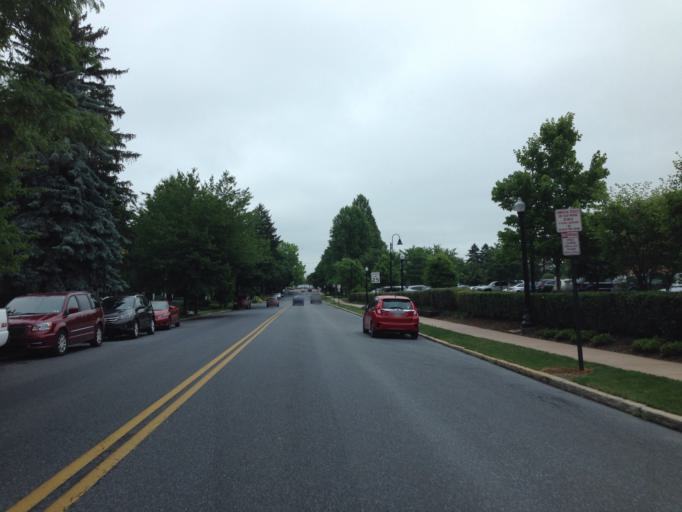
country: US
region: Pennsylvania
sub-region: Lancaster County
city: Lancaster
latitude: 40.0487
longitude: -76.3225
